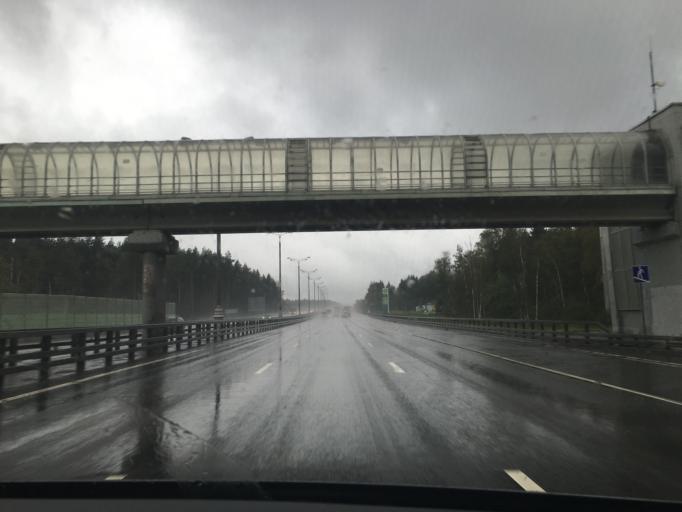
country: RU
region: Moskovskaya
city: Kokoshkino
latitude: 55.5536
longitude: 37.1392
